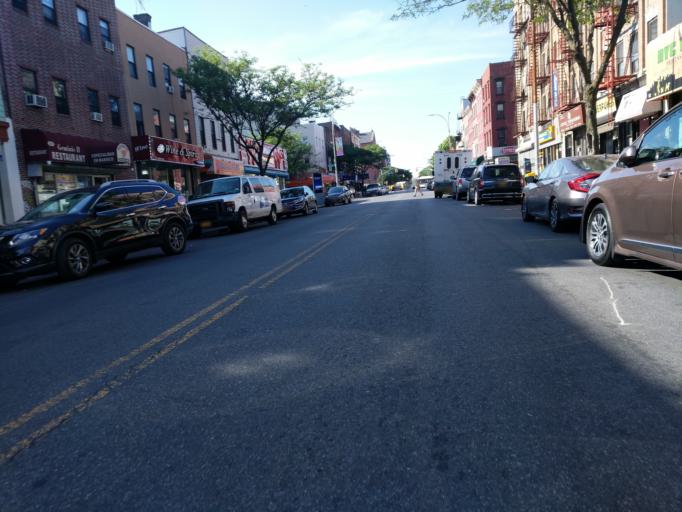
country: US
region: New York
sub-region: Queens County
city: Long Island City
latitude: 40.7053
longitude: -73.9429
